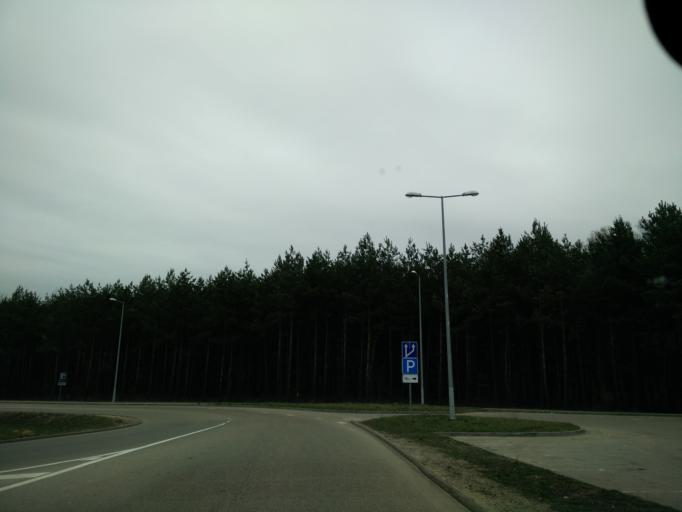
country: LT
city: Grigiskes
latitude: 54.6678
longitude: 25.1135
